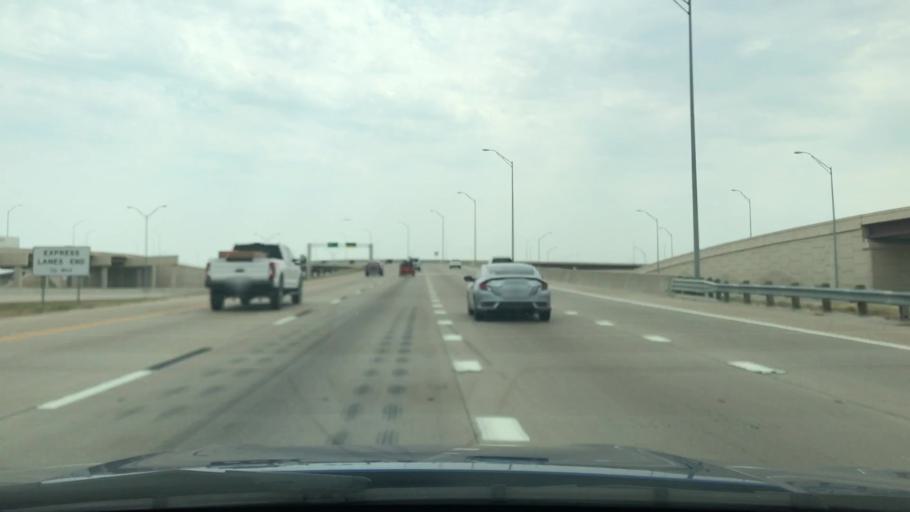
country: US
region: Texas
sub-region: Tarrant County
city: Grapevine
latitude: 32.9303
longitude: -97.0464
